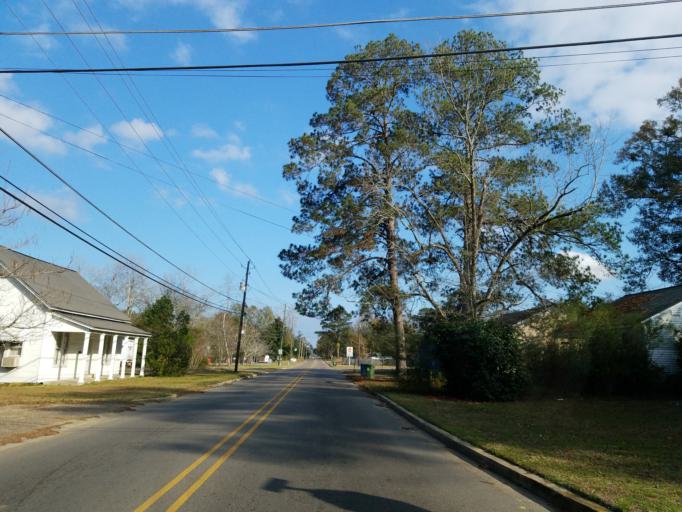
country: US
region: Mississippi
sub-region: Forrest County
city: Hattiesburg
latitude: 31.3357
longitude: -89.3179
